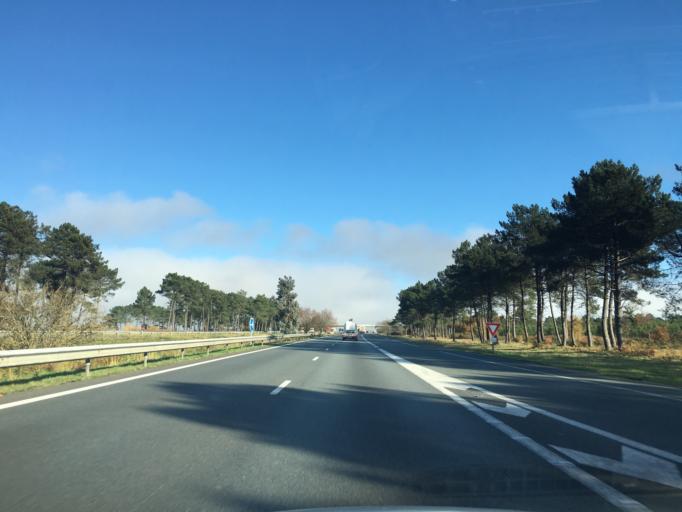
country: FR
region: Aquitaine
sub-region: Departement de la Gironde
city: Marcheprime
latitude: 44.6756
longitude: -0.8010
